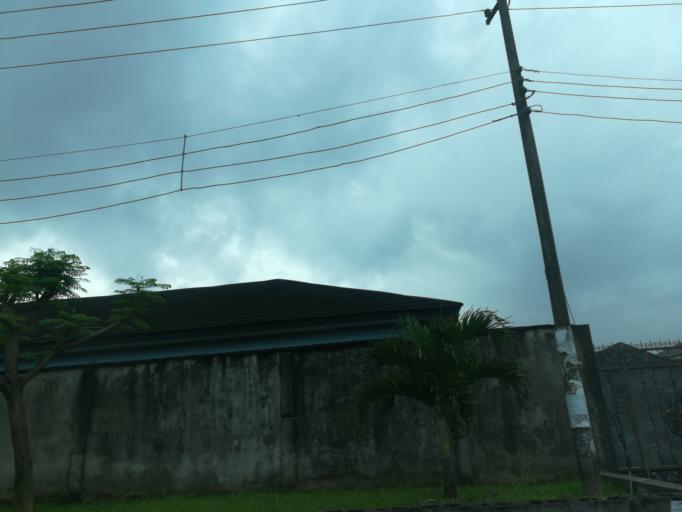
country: NG
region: Rivers
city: Port Harcourt
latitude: 4.8144
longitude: 7.0131
